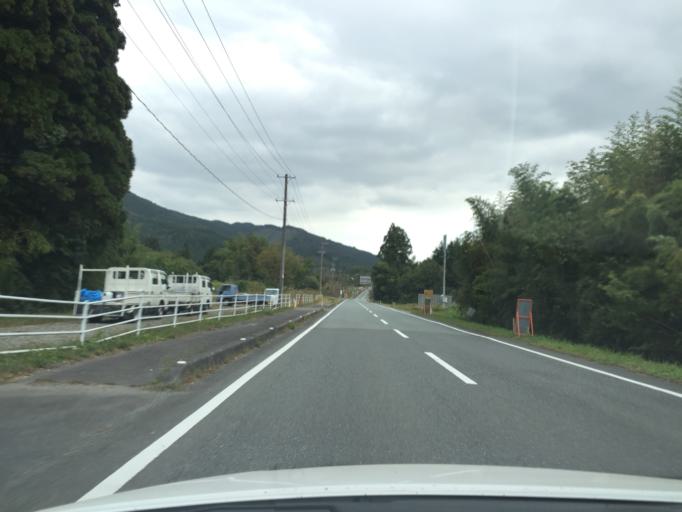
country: JP
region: Ibaraki
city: Kitaibaraki
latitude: 36.9327
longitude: 140.6865
